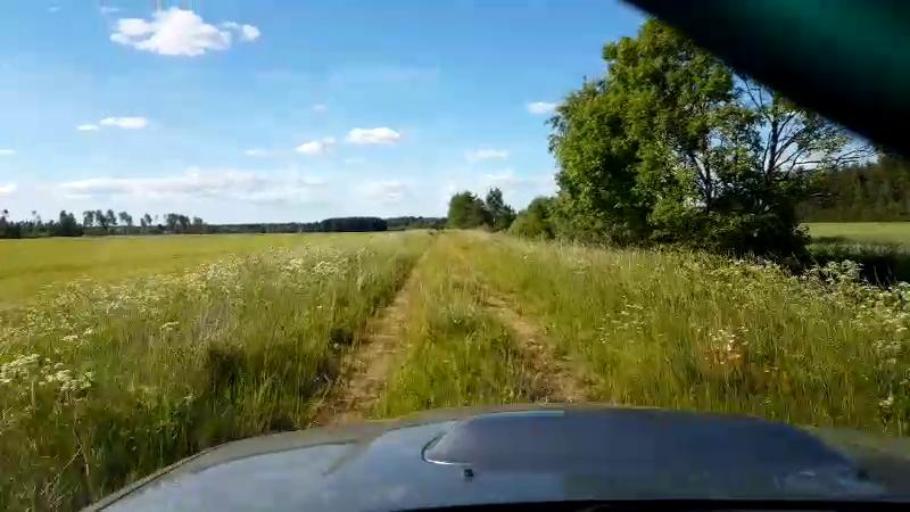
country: EE
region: Paernumaa
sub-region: Sauga vald
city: Sauga
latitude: 58.5008
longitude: 24.5910
